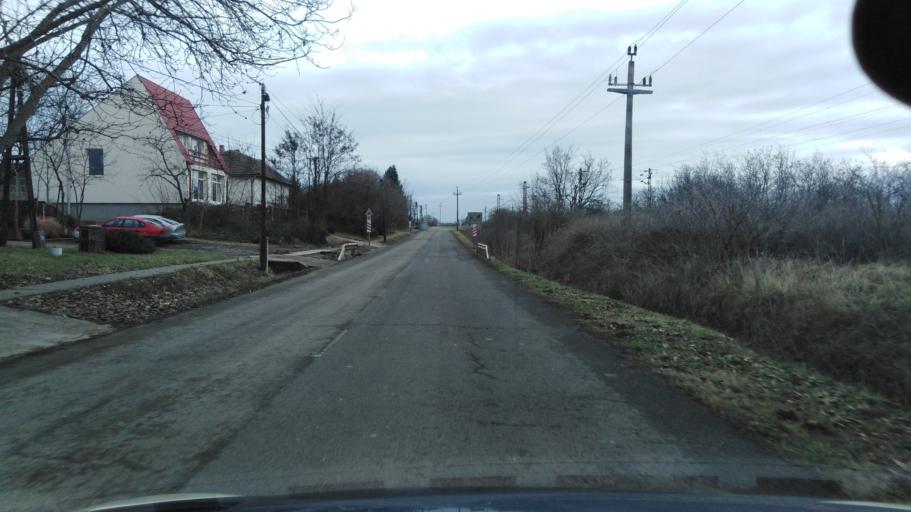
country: HU
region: Heves
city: Hatvan
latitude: 47.6723
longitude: 19.7014
